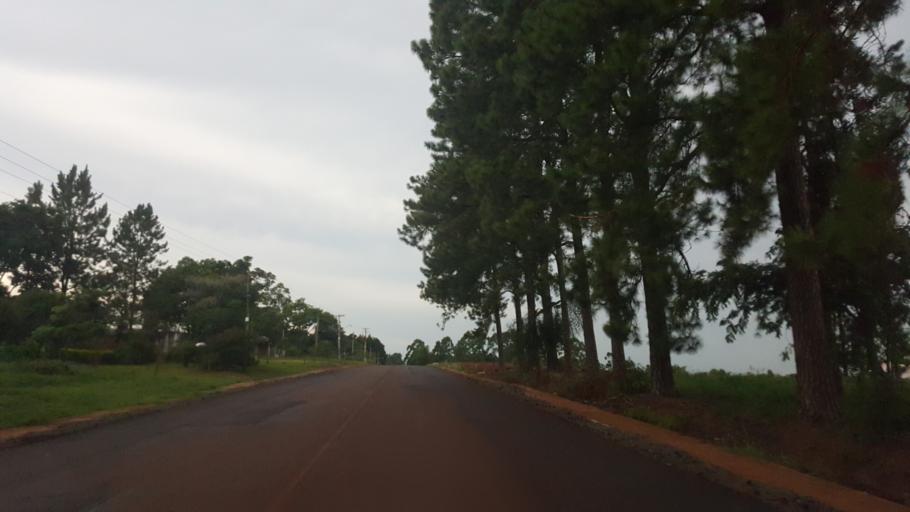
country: AR
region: Misiones
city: Puerto Leoni
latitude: -27.0017
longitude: -55.1641
